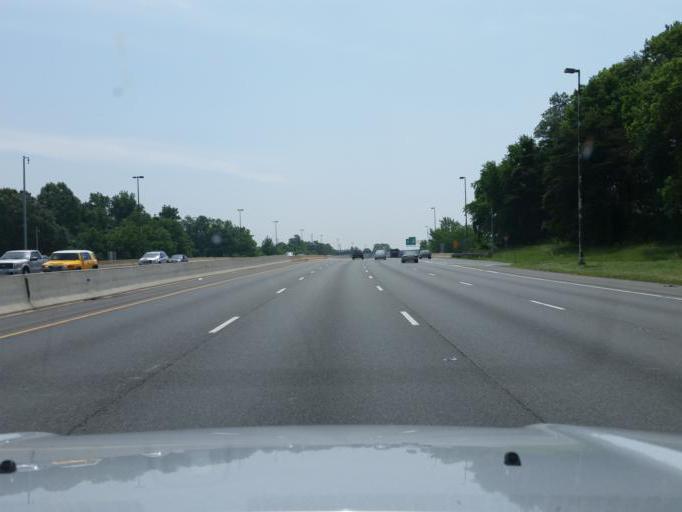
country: US
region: Maryland
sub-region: Montgomery County
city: Gaithersburg
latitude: 39.1499
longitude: -77.2179
